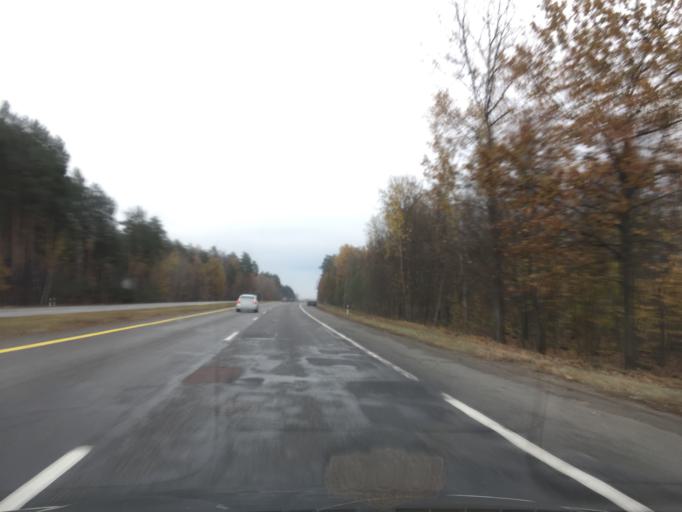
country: BY
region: Gomel
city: Horad Rechytsa
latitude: 52.3601
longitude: 30.6544
